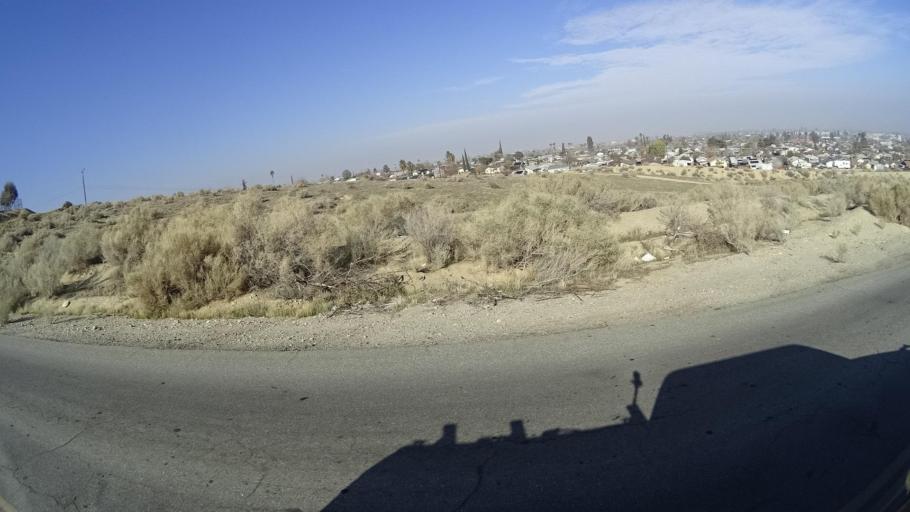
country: US
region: California
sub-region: Kern County
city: Taft Heights
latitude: 35.1301
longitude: -119.4673
